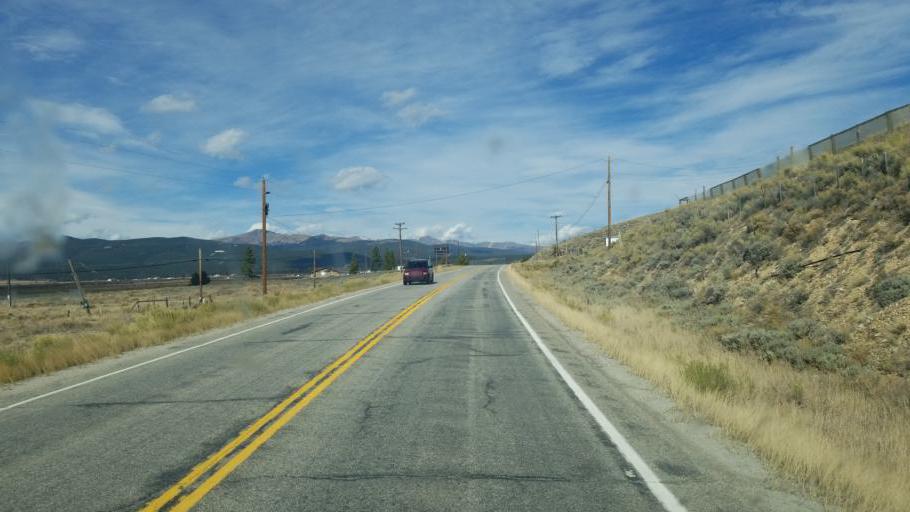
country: US
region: Colorado
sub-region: Lake County
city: Leadville North
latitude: 39.2047
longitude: -106.3444
